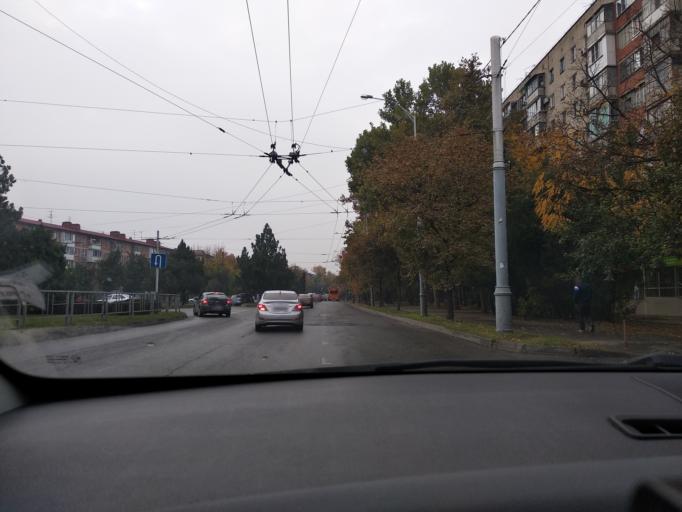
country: RU
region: Krasnodarskiy
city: Krasnodar
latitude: 45.0587
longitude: 38.9609
